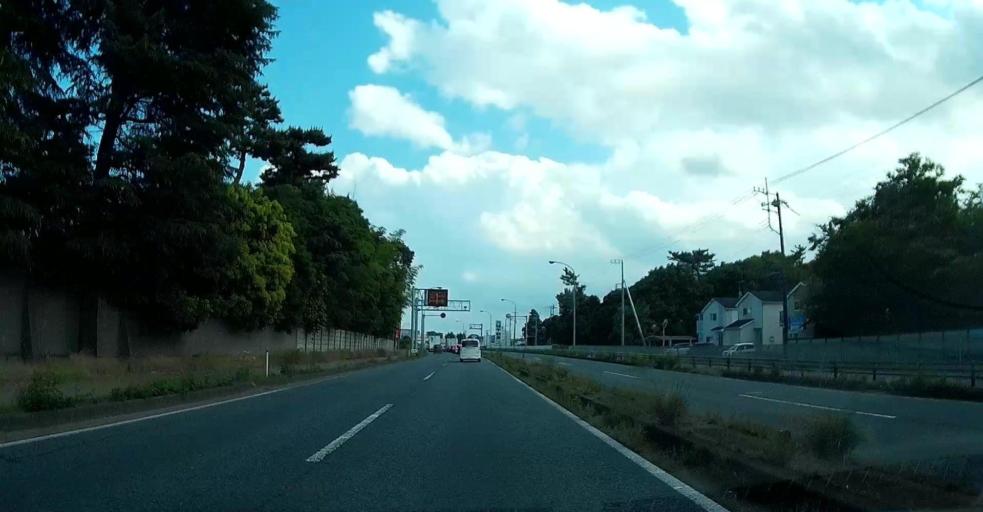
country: JP
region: Chiba
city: Noda
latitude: 35.9647
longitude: 139.8688
